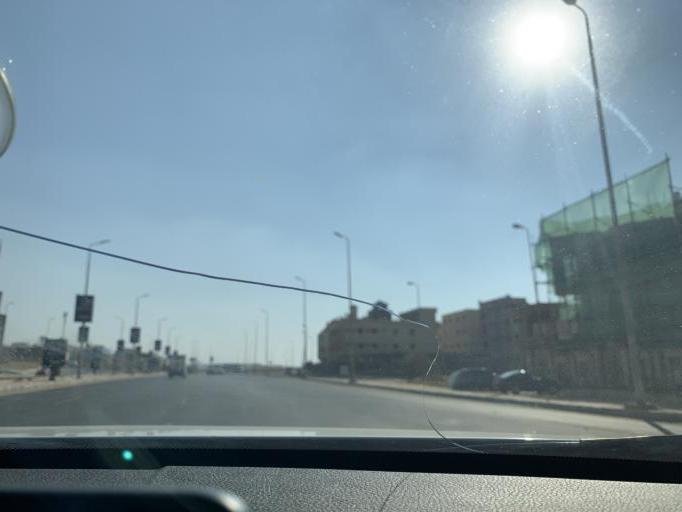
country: EG
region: Muhafazat al Qahirah
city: Cairo
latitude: 30.0019
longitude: 31.4687
